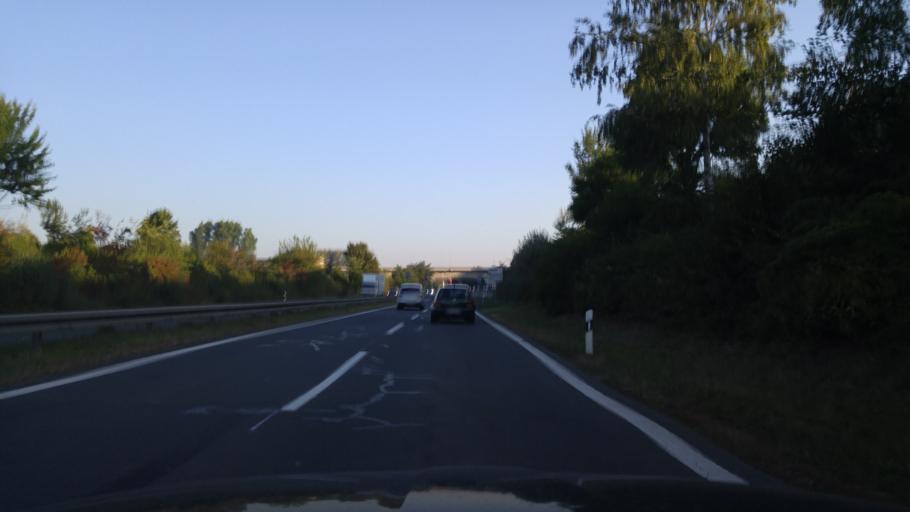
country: DE
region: Bavaria
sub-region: Regierungsbezirk Mittelfranken
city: Zirndorf
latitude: 49.4818
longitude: 10.9432
